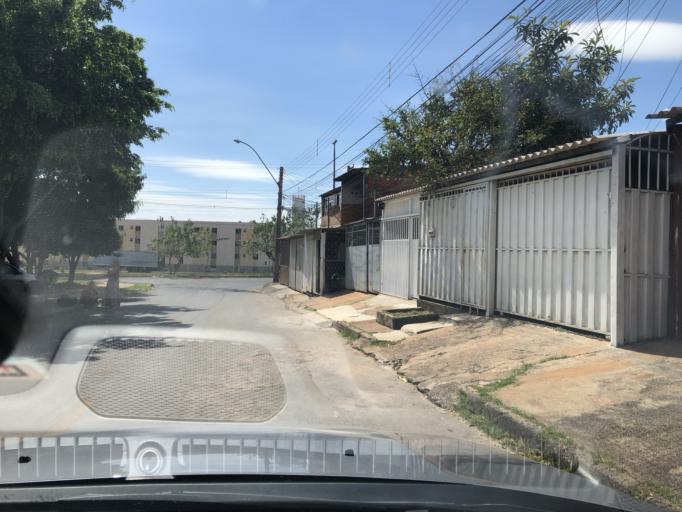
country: BR
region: Federal District
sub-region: Brasilia
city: Brasilia
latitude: -15.9005
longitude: -48.0422
